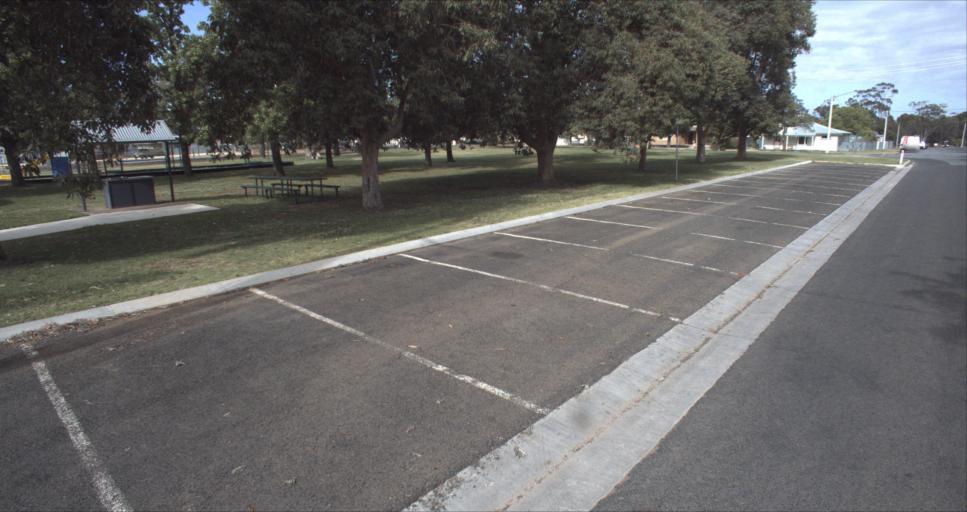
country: AU
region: New South Wales
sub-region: Leeton
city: Leeton
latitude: -34.5626
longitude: 146.4121
